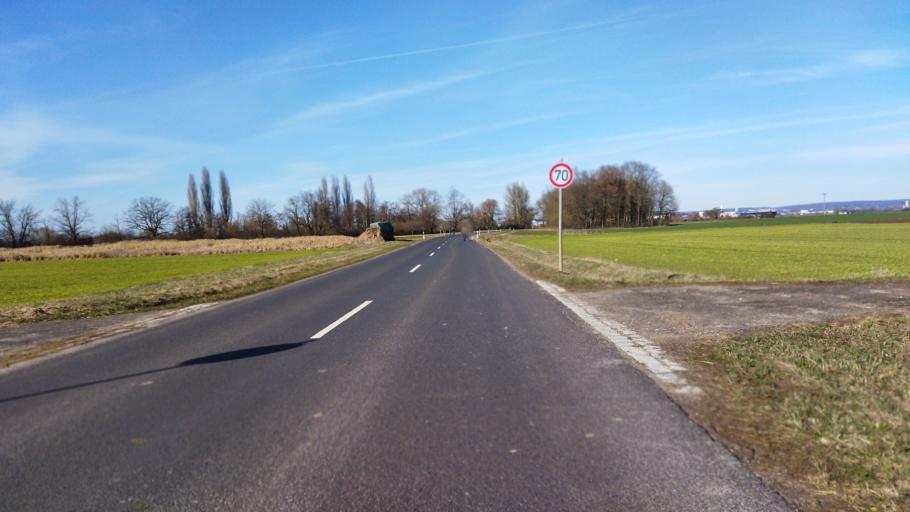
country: DE
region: Bavaria
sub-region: Regierungsbezirk Unterfranken
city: Grafenrheinfeld
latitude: 49.9868
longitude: 10.1993
